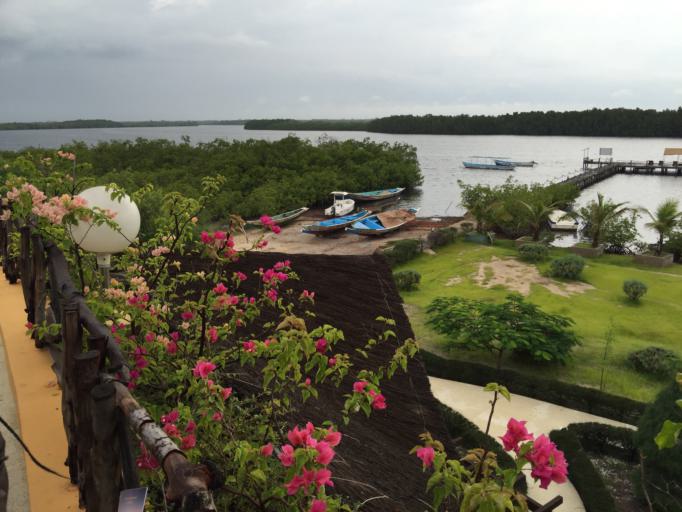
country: SN
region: Fatick
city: Sokone
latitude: 13.7874
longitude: -16.4783
